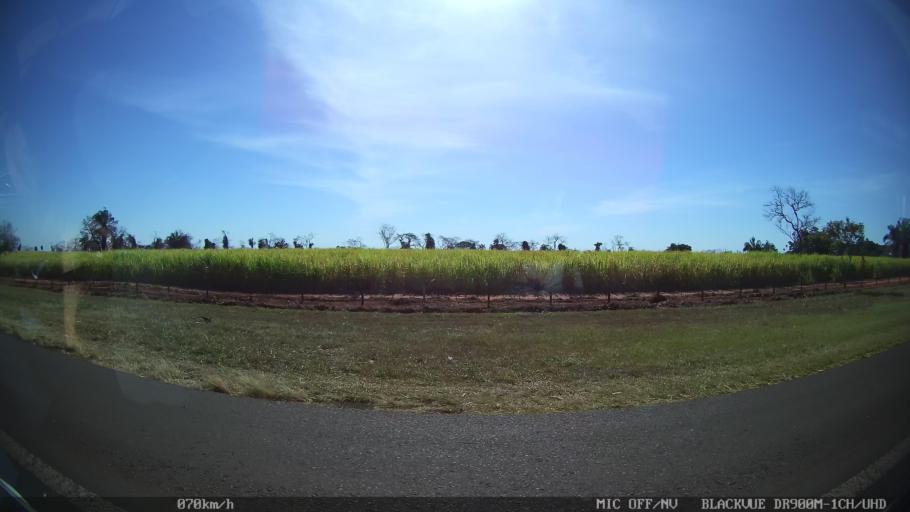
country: BR
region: Sao Paulo
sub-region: Barretos
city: Barretos
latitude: -20.5717
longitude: -48.6726
